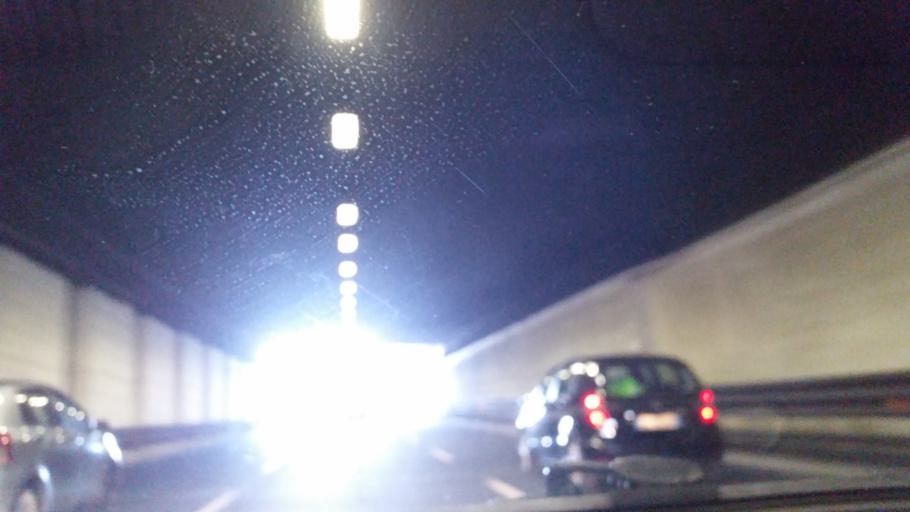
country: IT
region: Campania
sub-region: Provincia di Napoli
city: Napoli
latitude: 40.8525
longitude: 14.2167
